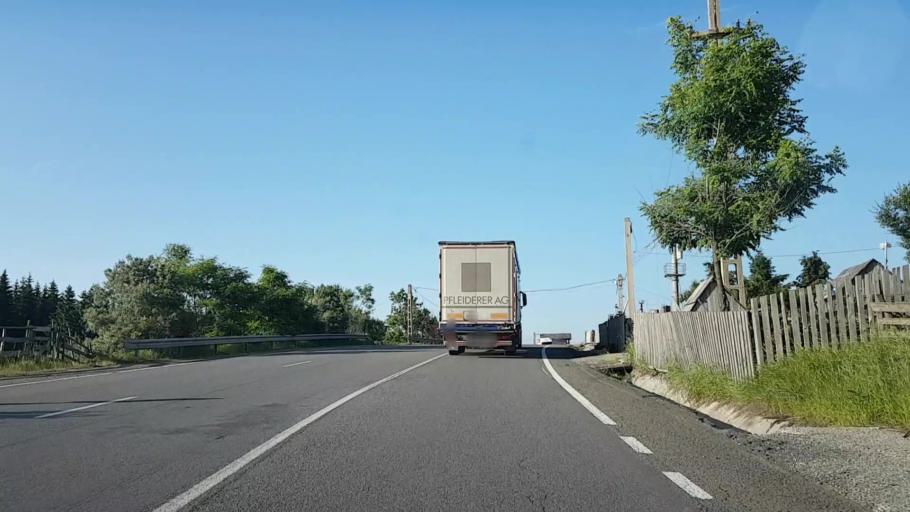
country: RO
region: Bistrita-Nasaud
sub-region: Comuna Lunca Ilvei
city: Lunca Ilvei
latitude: 47.2831
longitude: 25.0381
